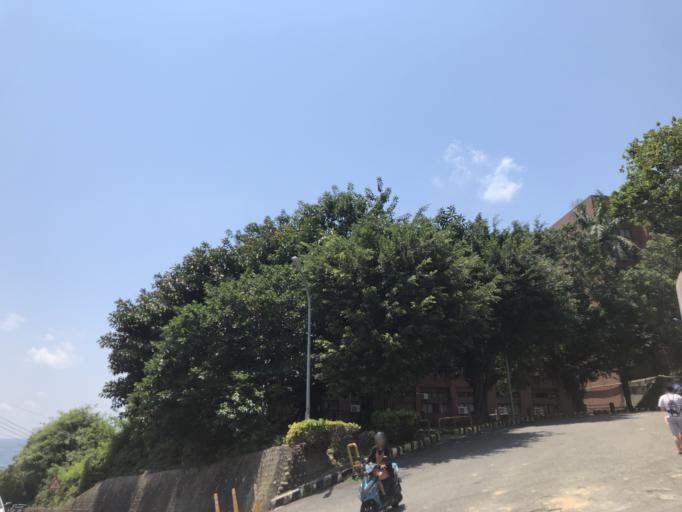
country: TW
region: Kaohsiung
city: Kaohsiung
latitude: 22.6289
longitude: 120.2646
